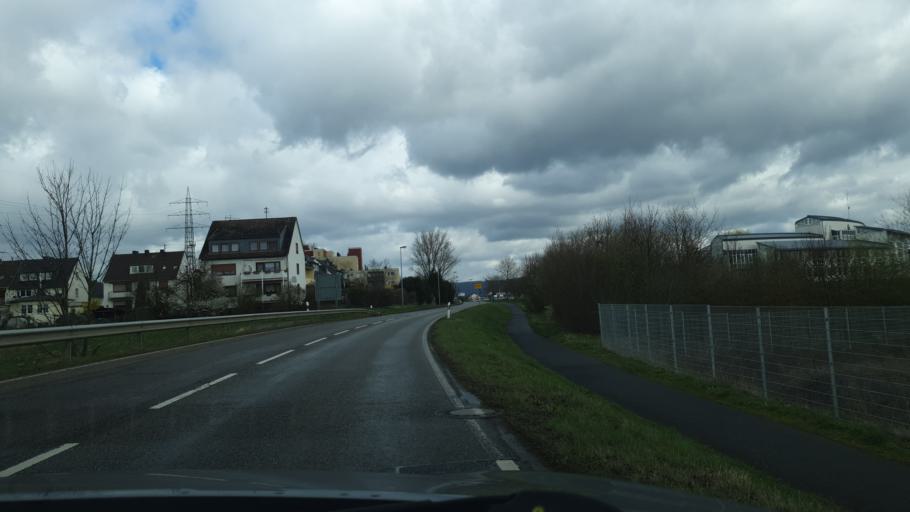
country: DE
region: Rheinland-Pfalz
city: Kettig
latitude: 50.4068
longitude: 7.4696
